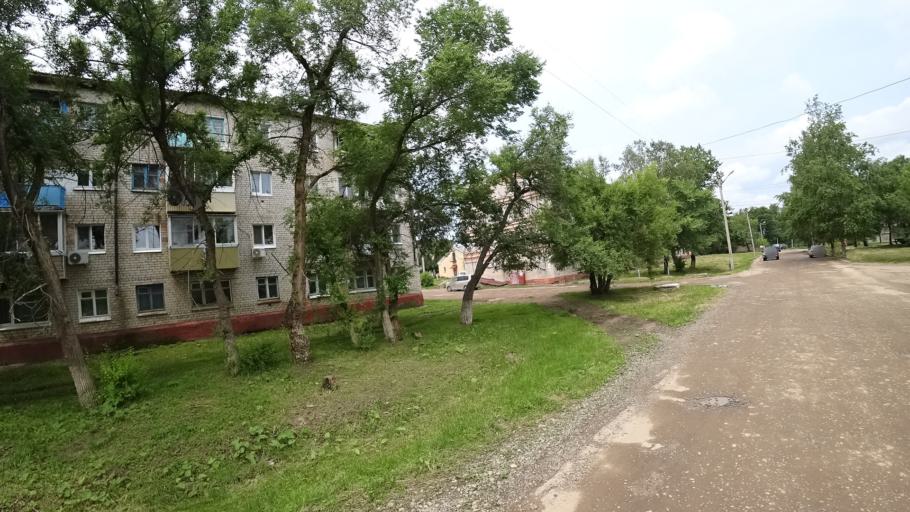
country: RU
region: Primorskiy
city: Novosysoyevka
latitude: 44.2279
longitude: 133.3612
